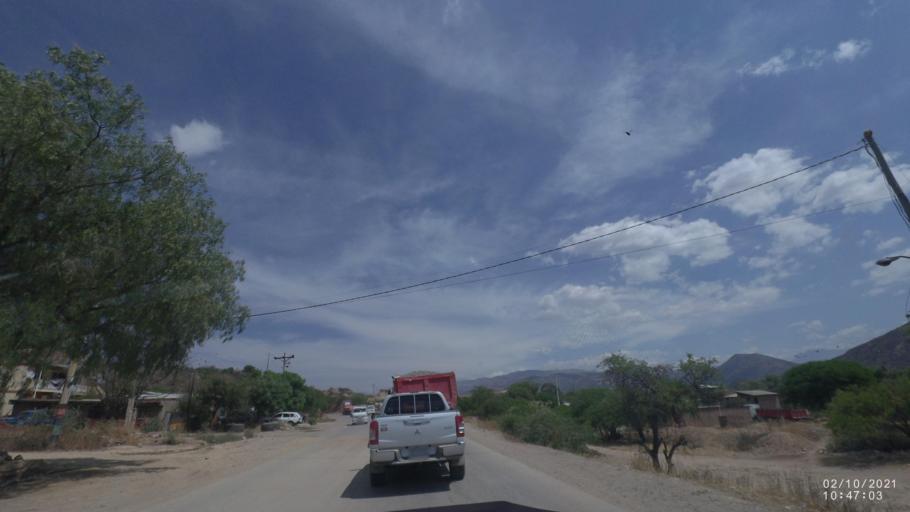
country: BO
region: Cochabamba
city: Capinota
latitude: -17.5834
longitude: -66.3274
